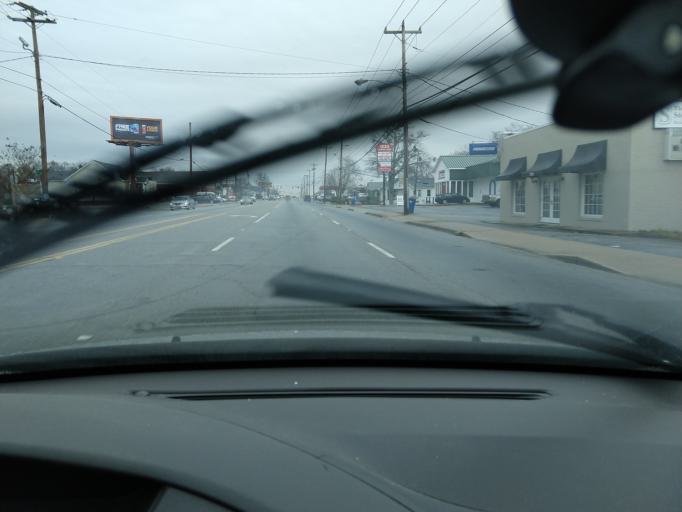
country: US
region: South Carolina
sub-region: Greenville County
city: Greenville
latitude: 34.8460
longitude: -82.3676
